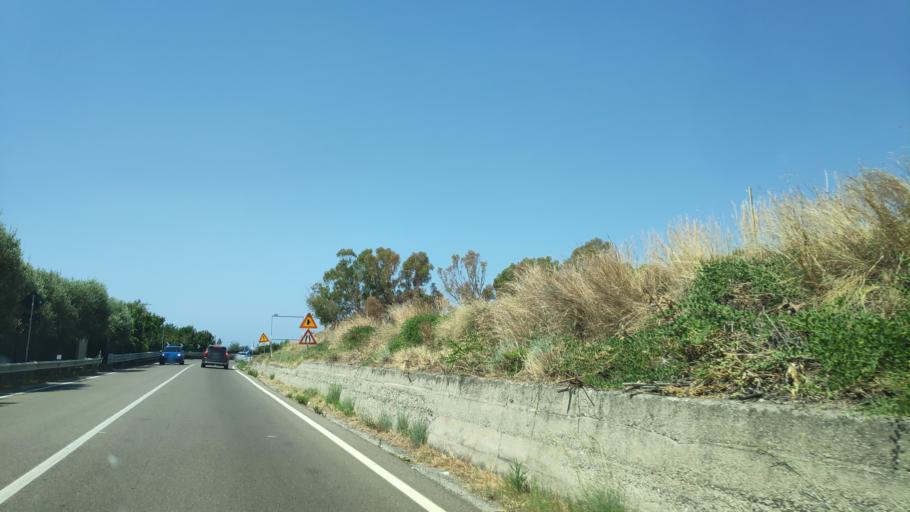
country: IT
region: Calabria
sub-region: Provincia di Reggio Calabria
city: Weather Station
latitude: 37.9235
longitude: 16.0461
